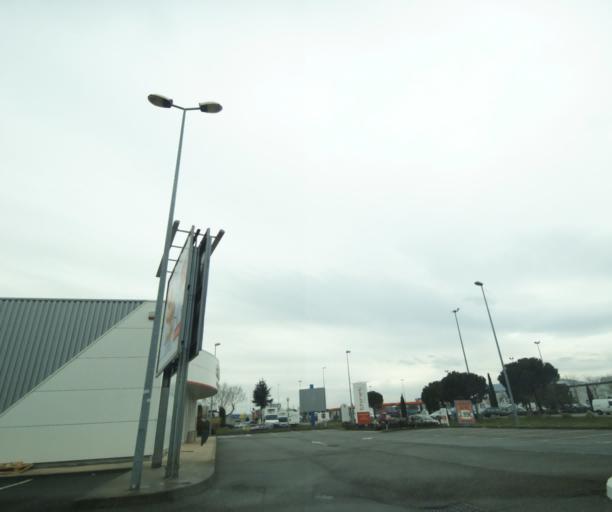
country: FR
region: Rhone-Alpes
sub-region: Departement de la Drome
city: Bourg-les-Valence
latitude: 44.9602
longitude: 4.8843
